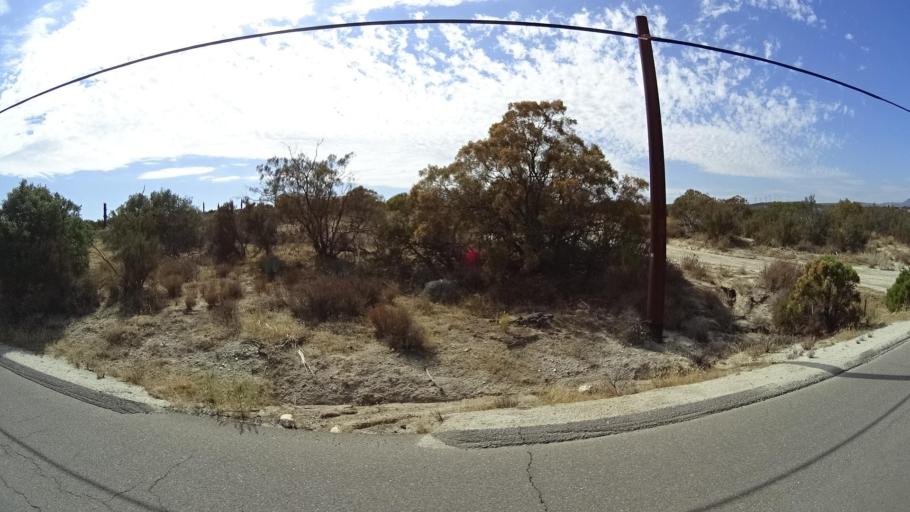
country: US
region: California
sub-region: San Diego County
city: Campo
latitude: 32.6840
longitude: -116.2936
